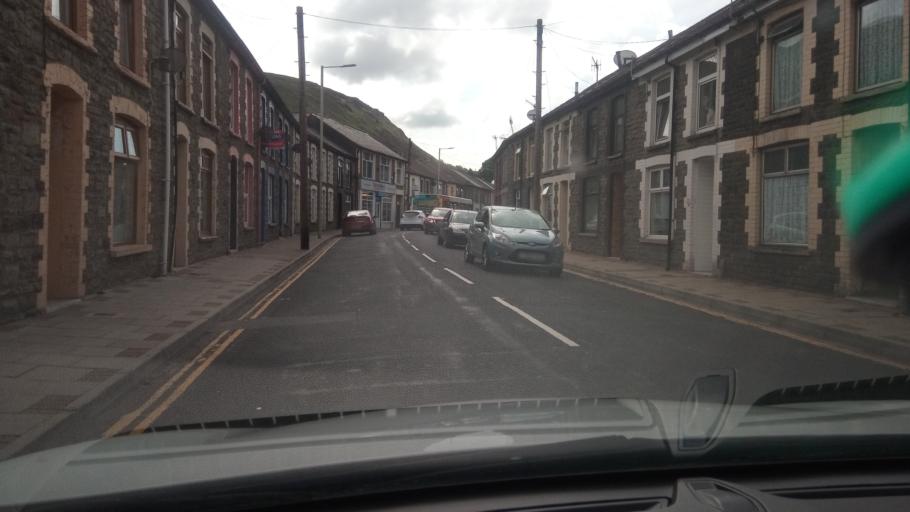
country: GB
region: Wales
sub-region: Rhondda Cynon Taf
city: Tonypandy
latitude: 51.6100
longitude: -3.4461
